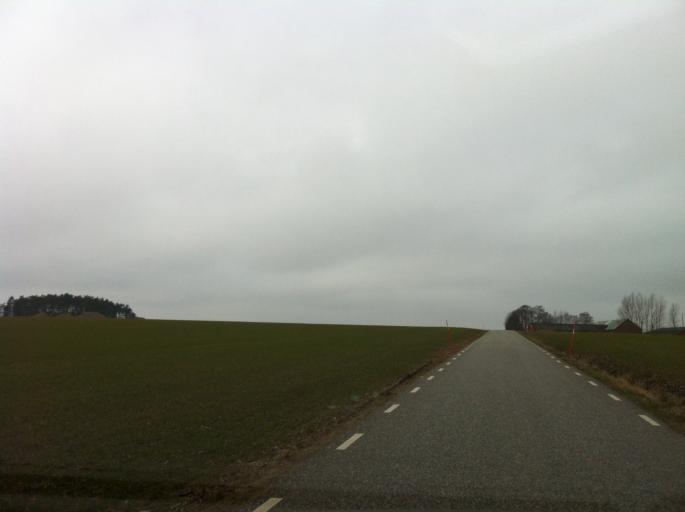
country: SE
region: Skane
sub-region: Kavlinge Kommun
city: Kaevlinge
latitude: 55.8046
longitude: 13.0927
